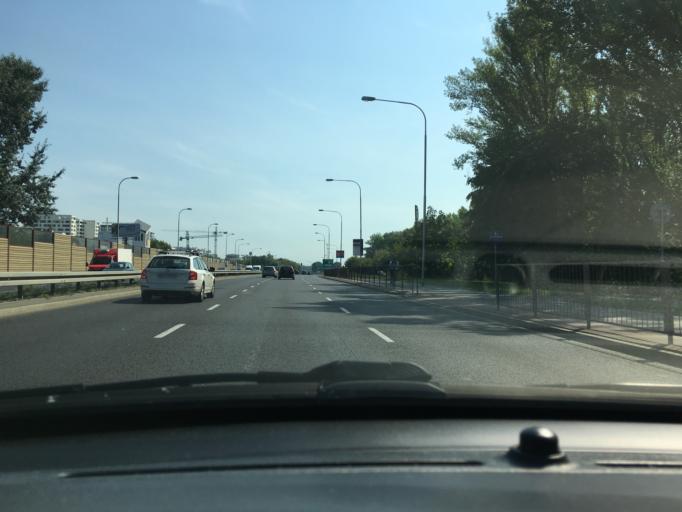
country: PL
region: Masovian Voivodeship
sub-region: Warszawa
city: Praga Poludnie
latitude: 52.2208
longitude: 21.0844
